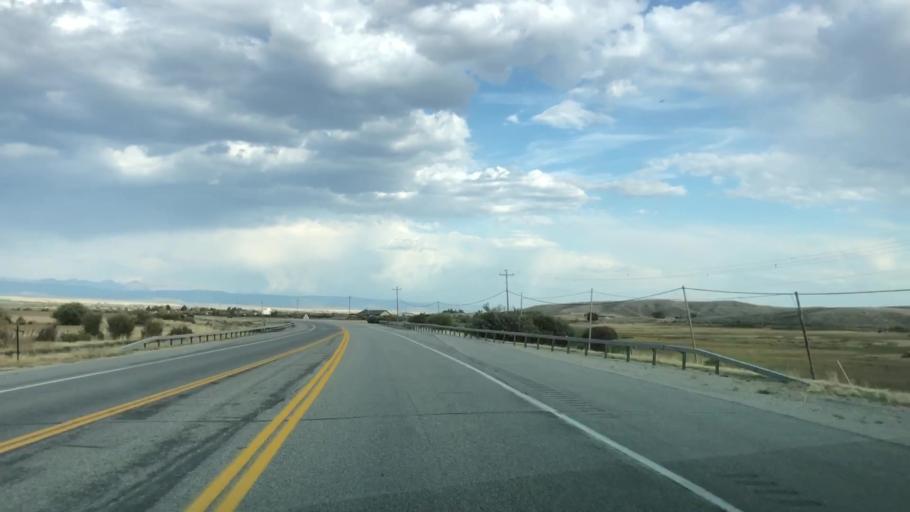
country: US
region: Wyoming
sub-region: Sublette County
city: Pinedale
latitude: 42.8669
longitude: -109.9229
